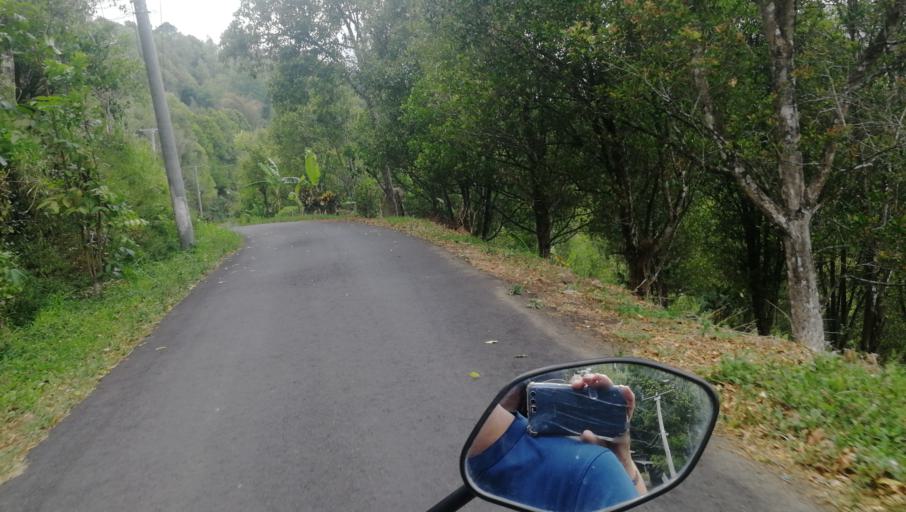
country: ID
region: Bali
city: Munduk
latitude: -8.2858
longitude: 115.0378
